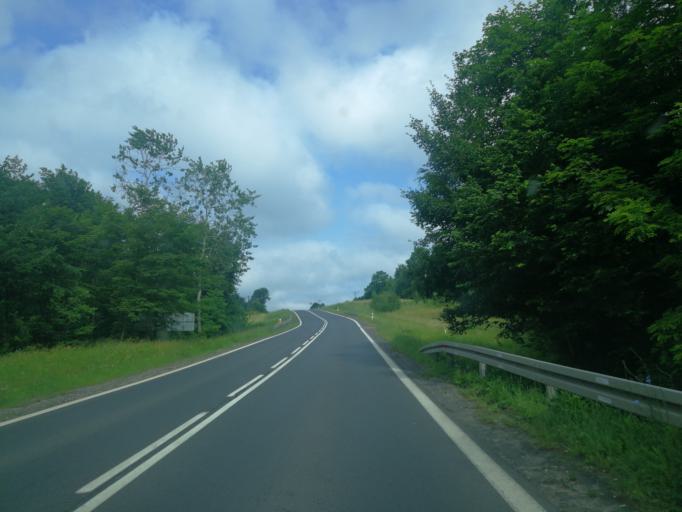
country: PL
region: Subcarpathian Voivodeship
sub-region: Powiat leski
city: Uherce Mineralne
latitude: 49.4671
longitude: 22.3848
